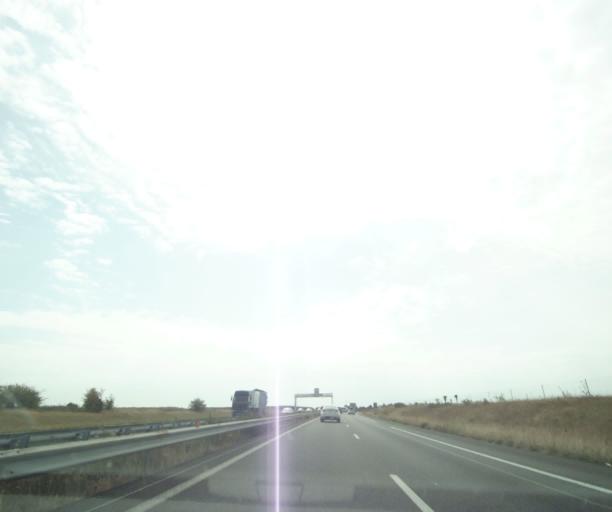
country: FR
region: Poitou-Charentes
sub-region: Departement de la Charente-Maritime
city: Saint-Jean-d'Angely
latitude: 45.9387
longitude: -0.5601
